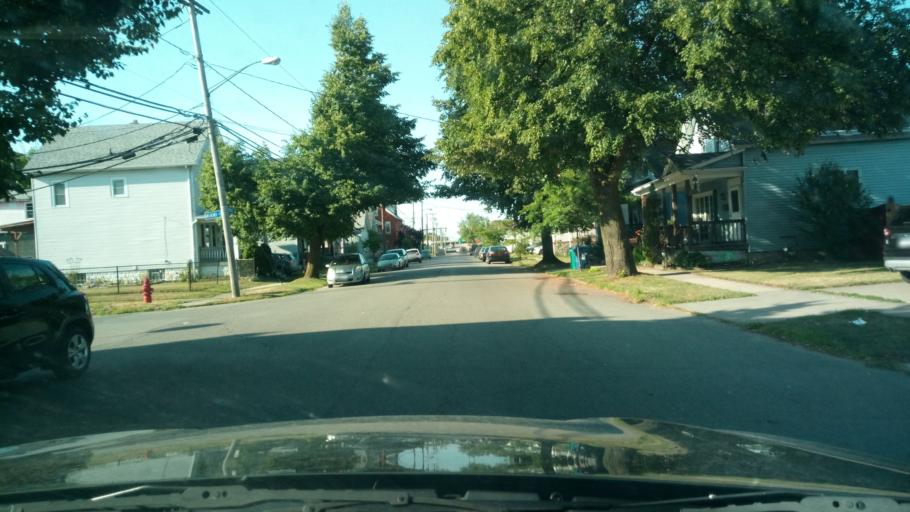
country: US
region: New York
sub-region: Erie County
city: Buffalo
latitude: 42.8693
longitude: -78.8587
